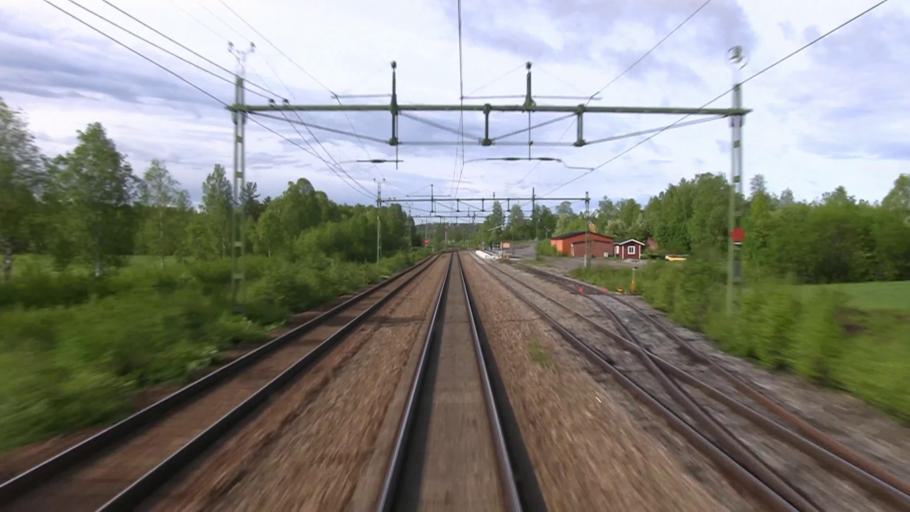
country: SE
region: Vaesterbotten
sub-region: Vindelns Kommun
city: Vindeln
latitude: 64.0991
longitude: 19.6769
